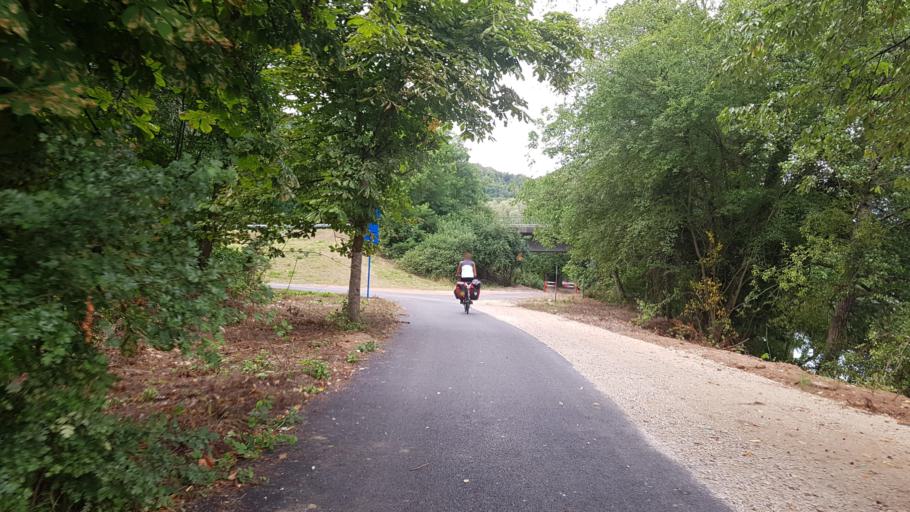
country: FR
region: Lorraine
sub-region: Departement de Meurthe-et-Moselle
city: Chaligny
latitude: 48.6338
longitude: 6.0435
